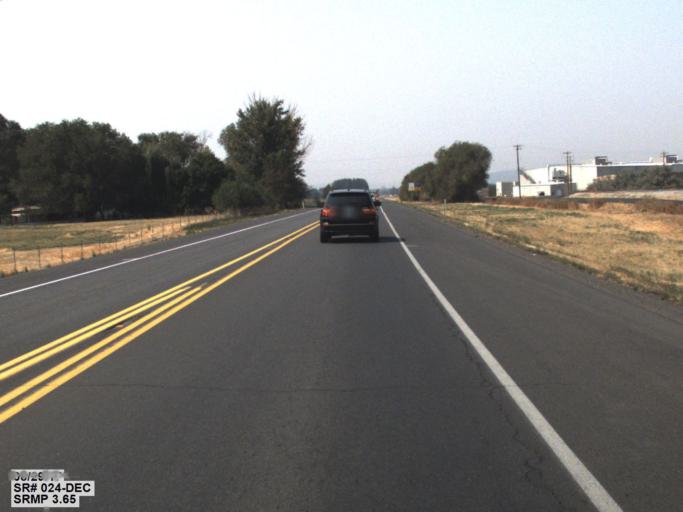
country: US
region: Washington
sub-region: Yakima County
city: Terrace Heights
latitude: 46.5633
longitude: -120.4065
